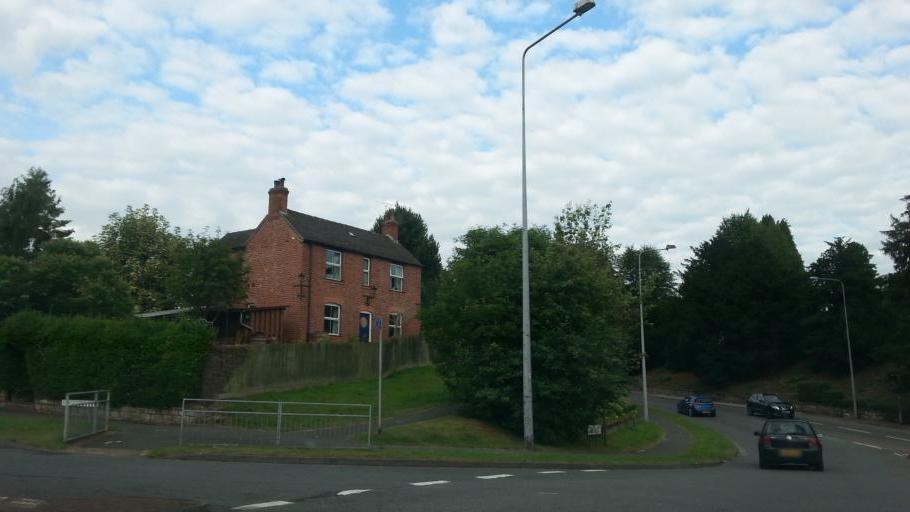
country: GB
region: England
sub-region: Staffordshire
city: Uttoxeter
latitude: 52.8939
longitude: -1.8713
